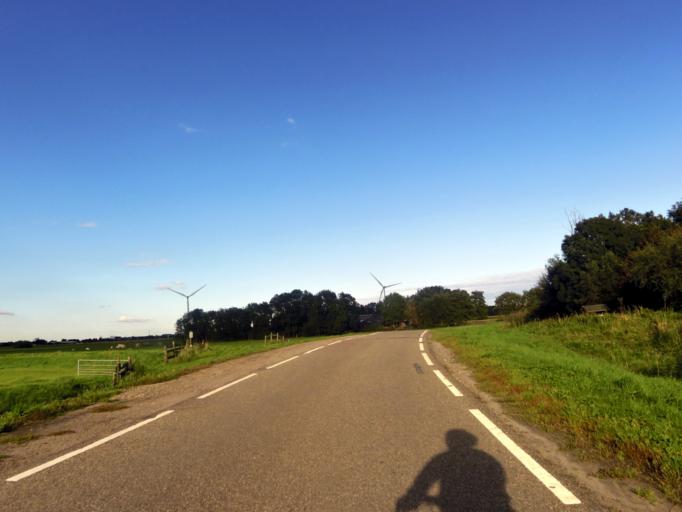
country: NL
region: South Holland
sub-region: Gemeente Alphen aan den Rijn
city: Alphen aan den Rijn
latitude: 52.1171
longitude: 4.6098
